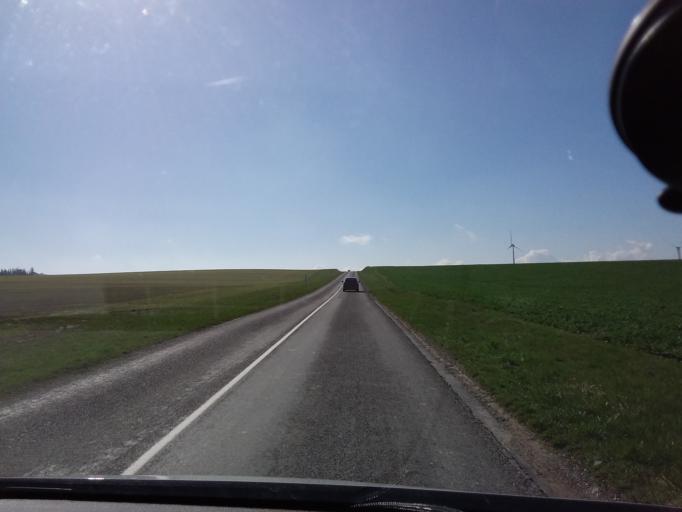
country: FR
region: Picardie
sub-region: Departement de l'Aisne
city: Guignicourt
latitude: 49.5238
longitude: 4.0440
